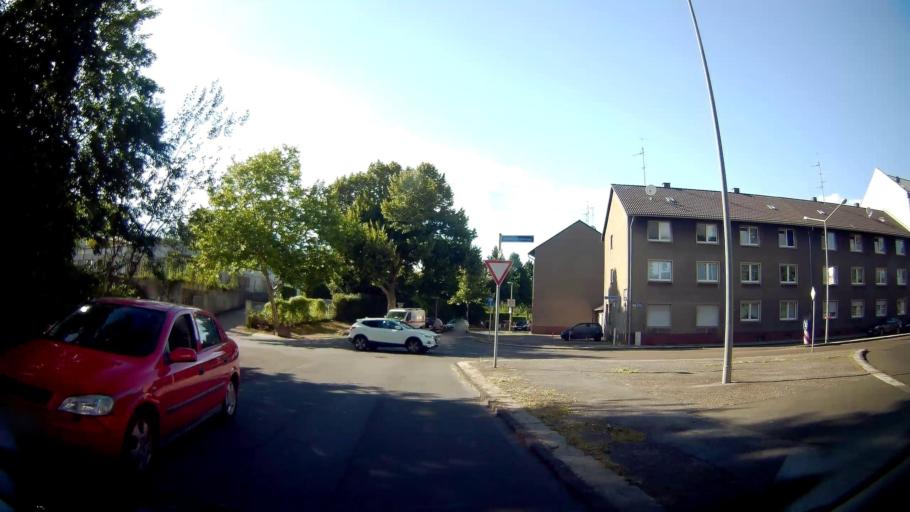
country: DE
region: North Rhine-Westphalia
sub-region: Regierungsbezirk Dusseldorf
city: Essen
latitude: 51.4730
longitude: 6.9967
